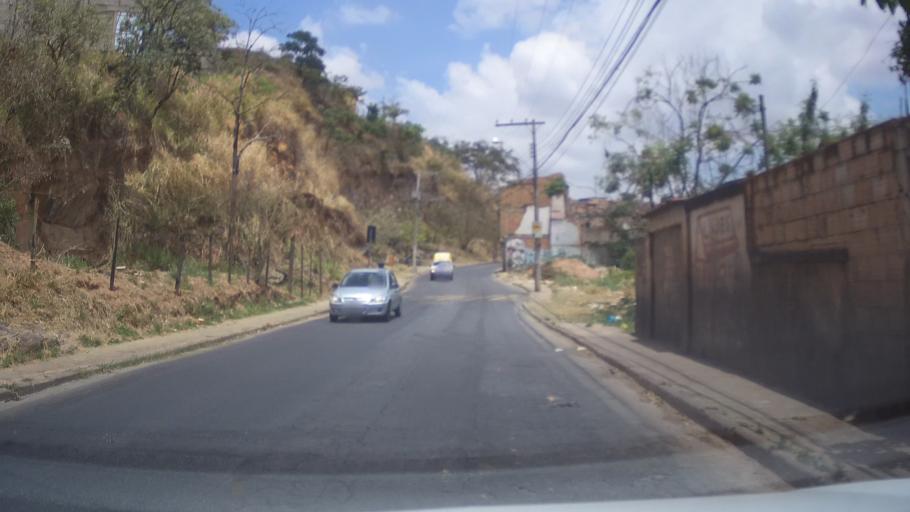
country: BR
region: Minas Gerais
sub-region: Belo Horizonte
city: Belo Horizonte
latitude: -19.9052
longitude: -43.8843
